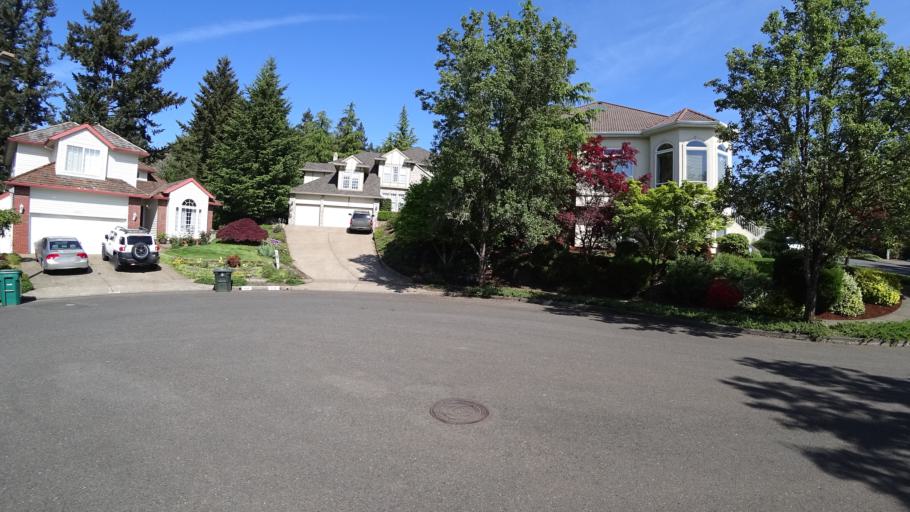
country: US
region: Oregon
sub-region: Washington County
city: Aloha
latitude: 45.4726
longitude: -122.8472
